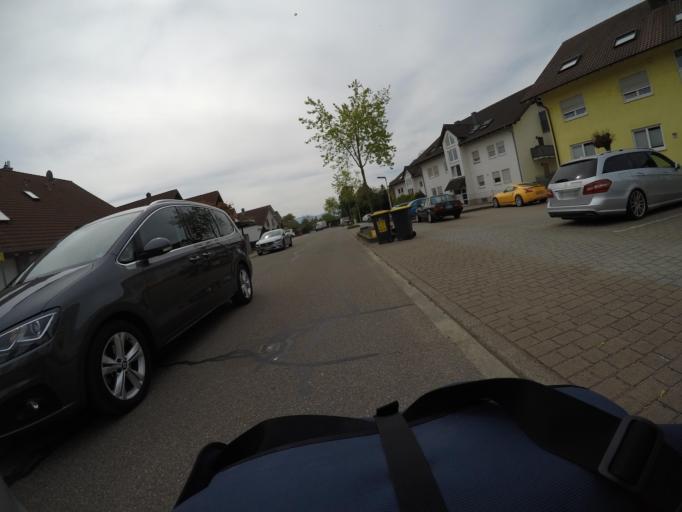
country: DE
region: Baden-Wuerttemberg
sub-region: Karlsruhe Region
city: Hugelsheim
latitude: 48.7928
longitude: 8.1099
